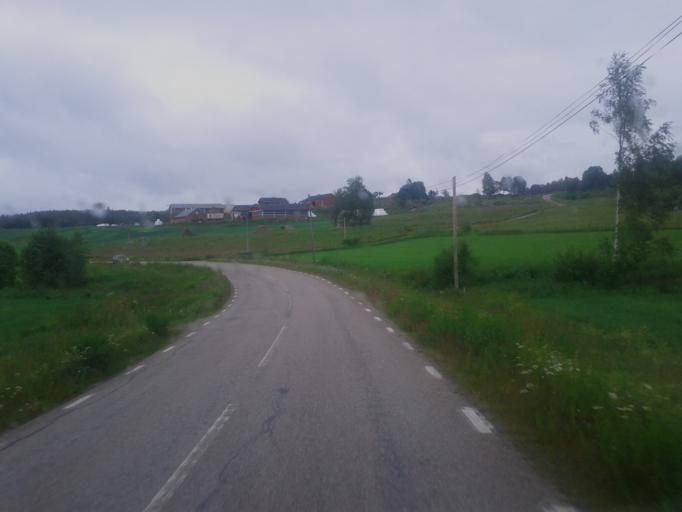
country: SE
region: Gaevleborg
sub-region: Nordanstigs Kommun
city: Bergsjoe
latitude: 61.9765
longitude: 17.2894
